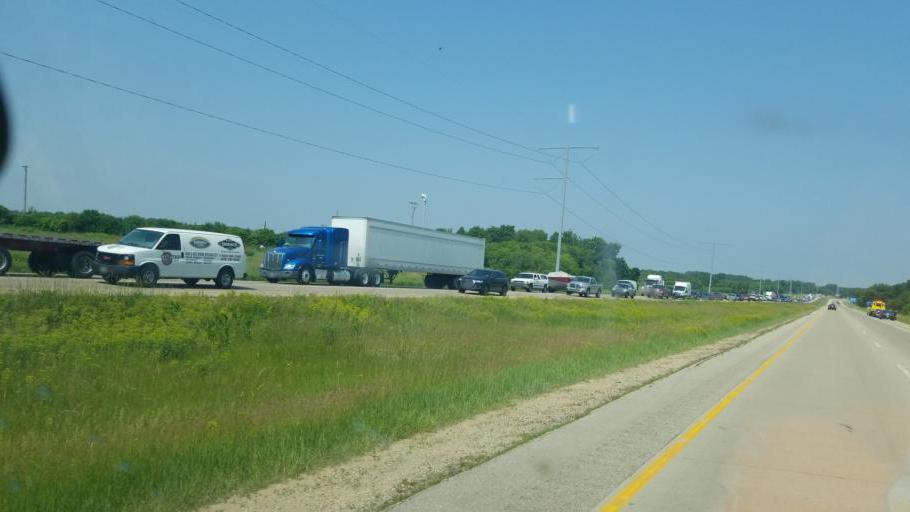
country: US
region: Wisconsin
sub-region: Dane County
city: McFarland
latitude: 43.0326
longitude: -89.2630
